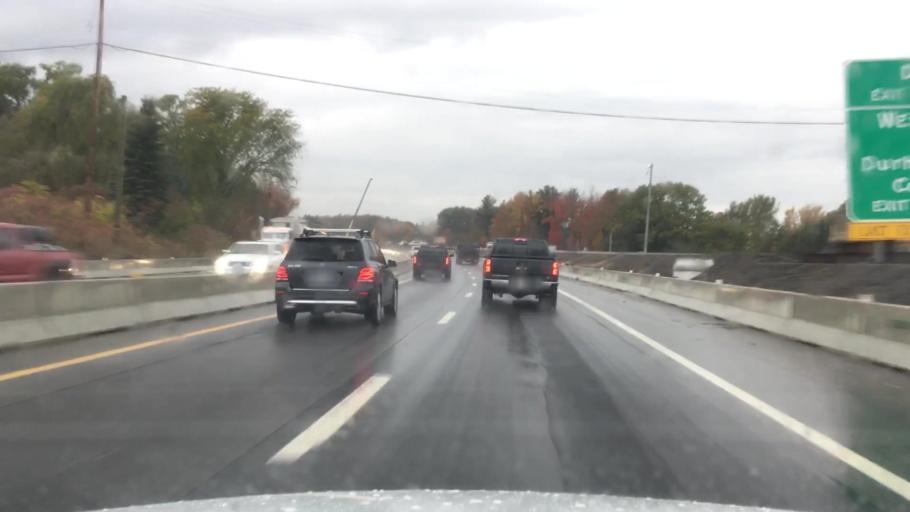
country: US
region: Maine
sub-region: York County
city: Eliot
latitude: 43.1226
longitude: -70.8308
